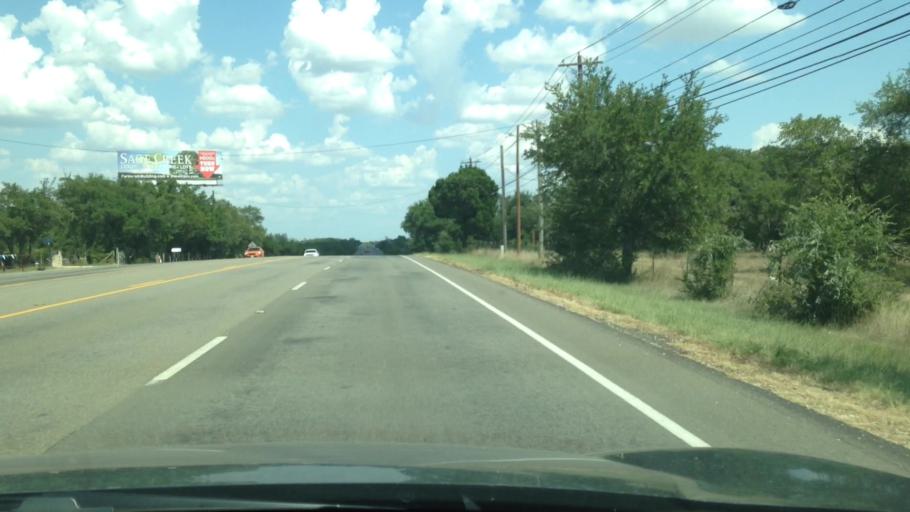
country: US
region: Texas
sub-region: Williamson County
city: Leander
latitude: 30.6339
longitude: -97.7745
